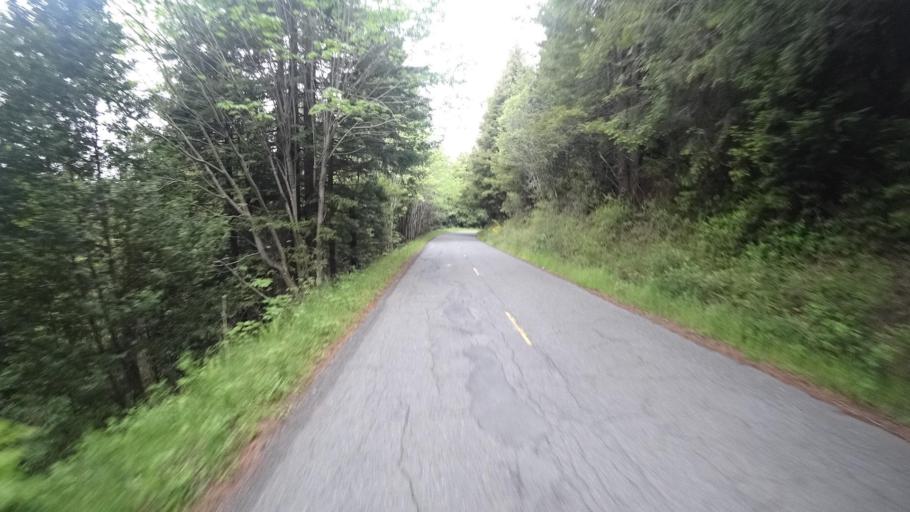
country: US
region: California
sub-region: Humboldt County
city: Blue Lake
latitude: 40.8733
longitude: -123.9756
